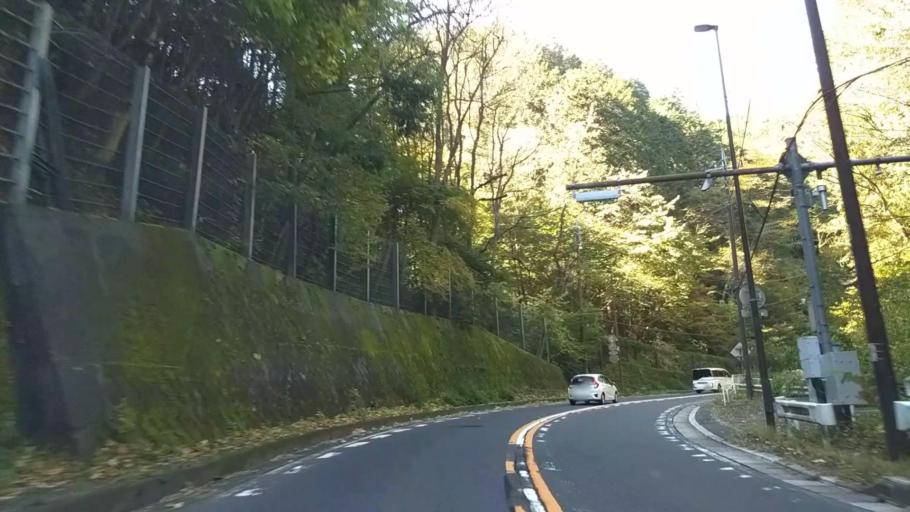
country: JP
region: Tokyo
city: Hachioji
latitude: 35.6190
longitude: 139.2318
